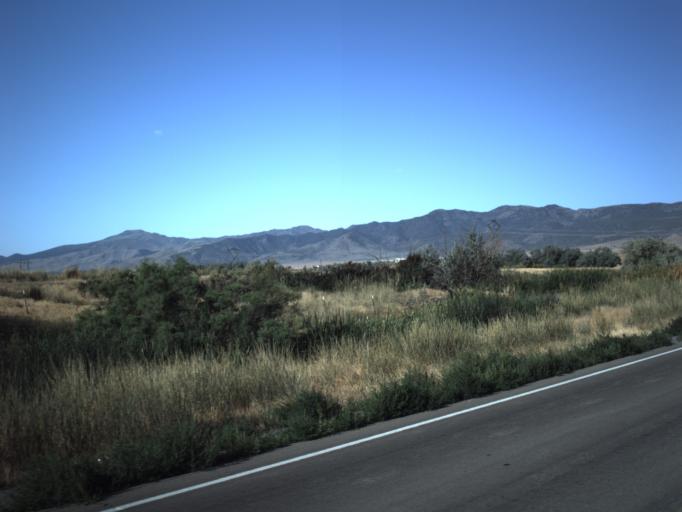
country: US
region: Utah
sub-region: Utah County
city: Genola
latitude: 39.9523
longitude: -111.9325
